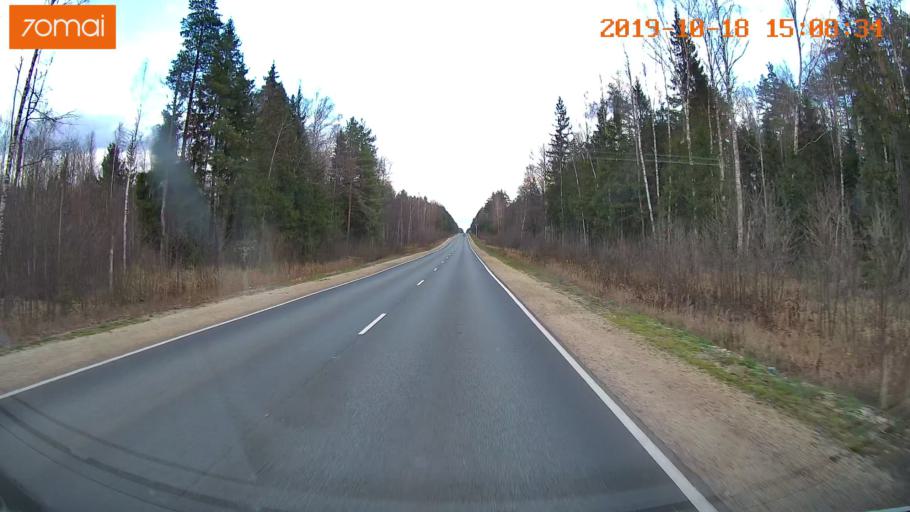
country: RU
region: Vladimir
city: Gus'-Khrustal'nyy
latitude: 55.5542
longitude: 40.6119
